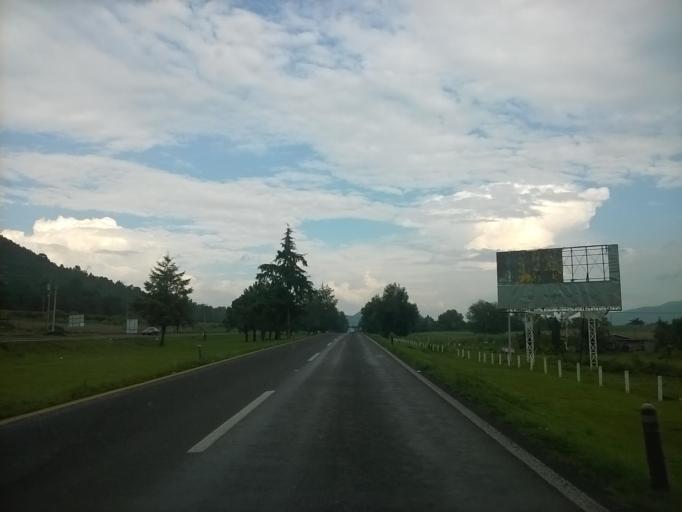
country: MX
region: Michoacan
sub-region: Huiramba
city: El Pedregal
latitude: 19.5314
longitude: -101.4874
